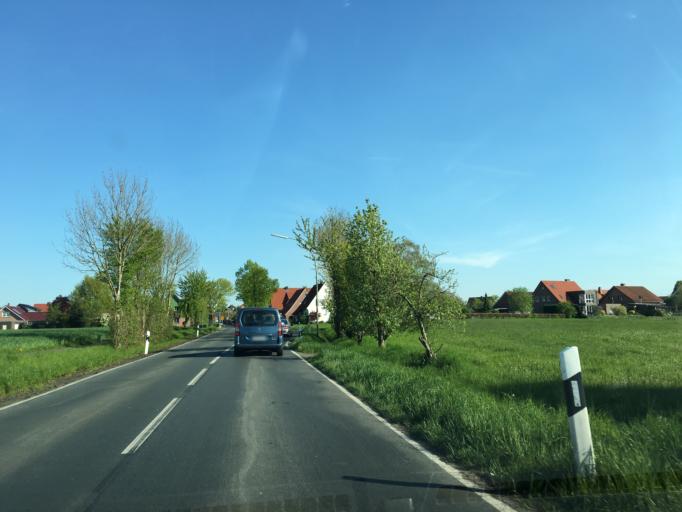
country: DE
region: North Rhine-Westphalia
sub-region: Regierungsbezirk Munster
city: Senden
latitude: 51.8266
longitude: 7.5296
